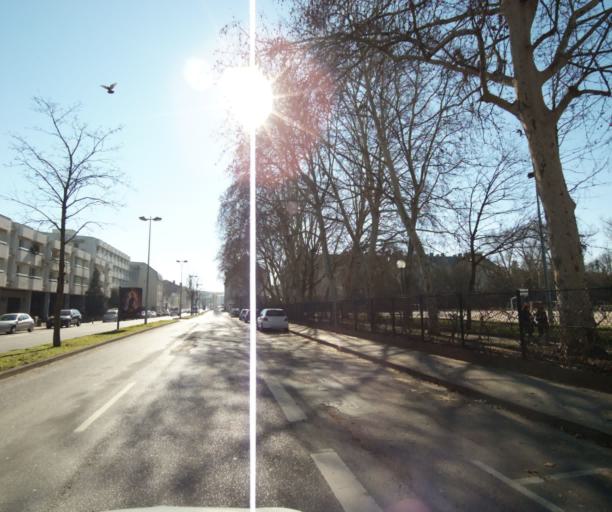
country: FR
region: Lorraine
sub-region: Departement de Meurthe-et-Moselle
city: Nancy
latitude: 48.6980
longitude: 6.1882
